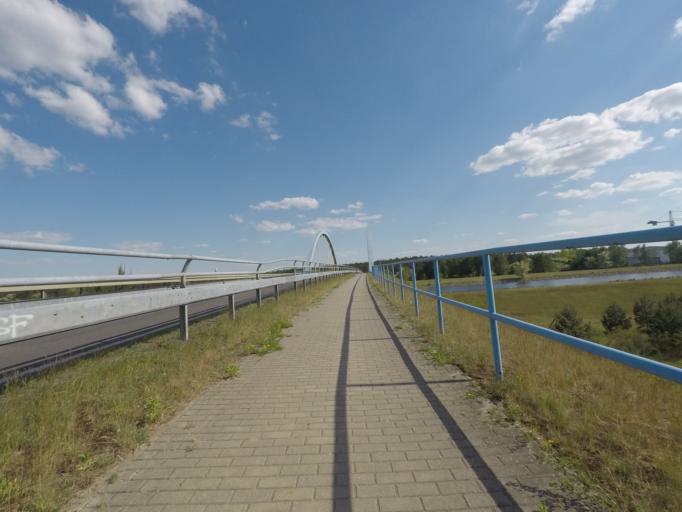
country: DE
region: Brandenburg
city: Eberswalde
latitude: 52.8550
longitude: 13.7979
